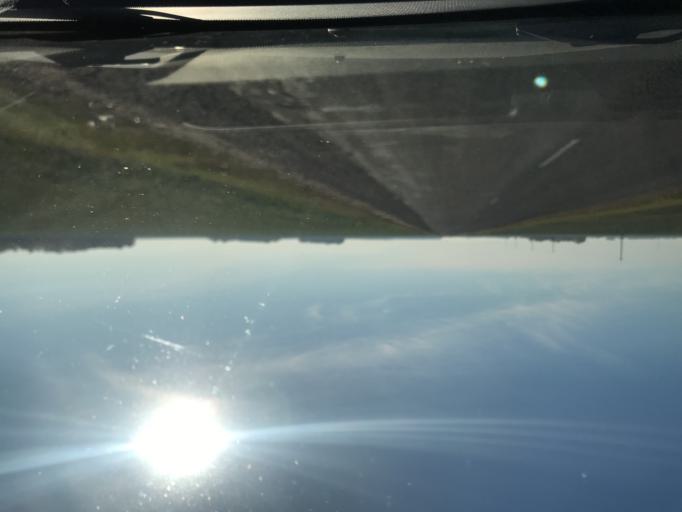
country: BY
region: Gomel
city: Brahin
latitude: 51.7961
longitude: 30.1499
